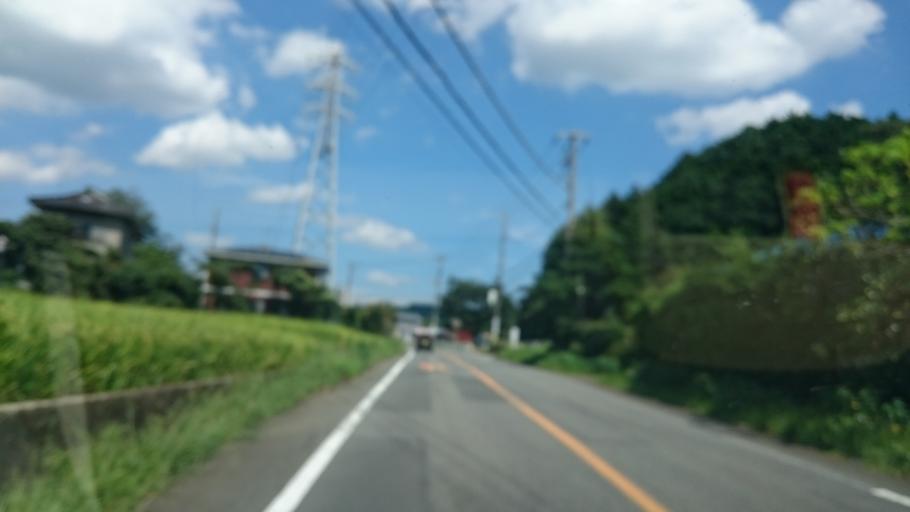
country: JP
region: Shizuoka
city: Mishima
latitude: 35.1900
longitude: 138.9220
